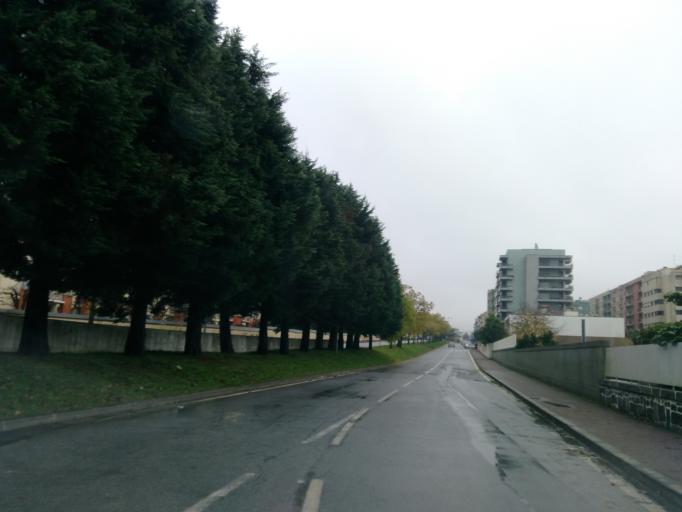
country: PT
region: Braga
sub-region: Braga
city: Braga
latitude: 41.5558
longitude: -8.3950
